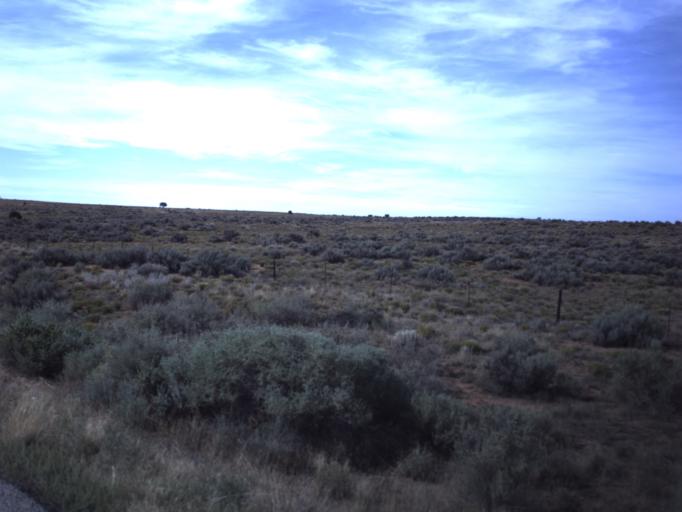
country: US
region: Utah
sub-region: San Juan County
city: Blanding
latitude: 37.3589
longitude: -109.3457
